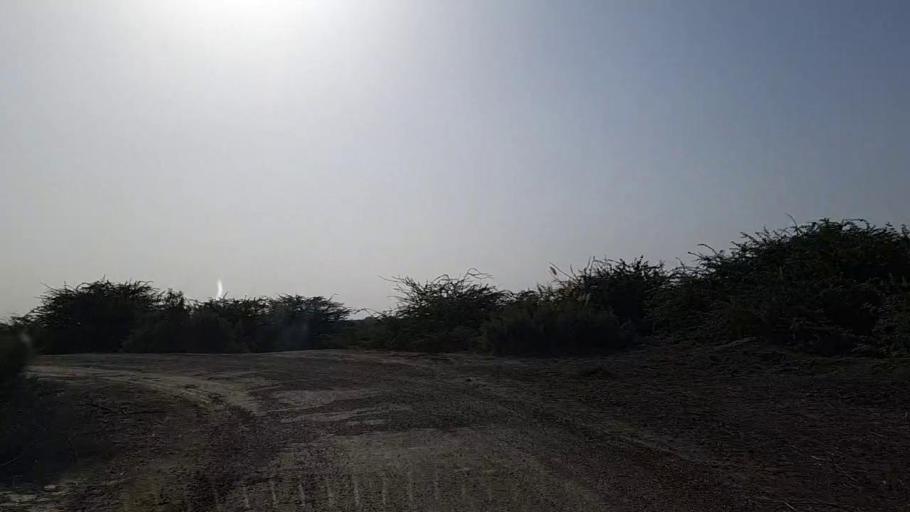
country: PK
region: Sindh
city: Jati
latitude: 24.2820
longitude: 68.2296
